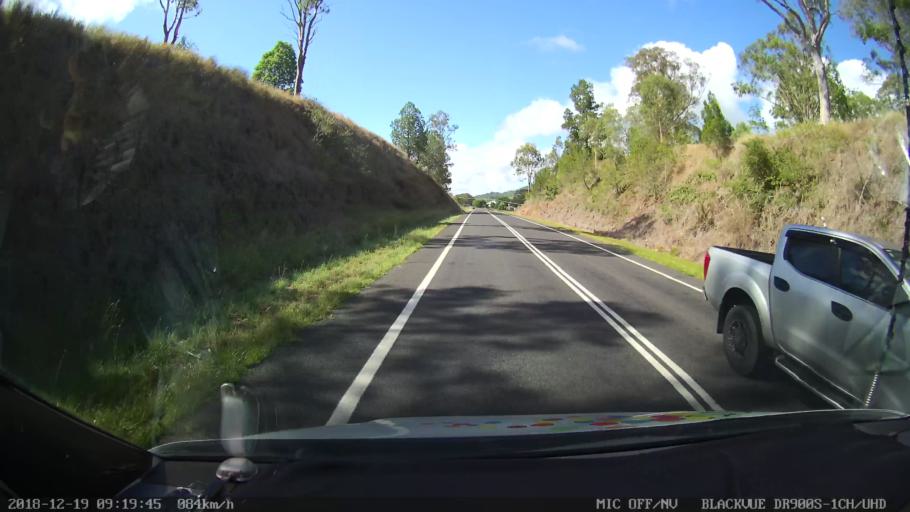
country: AU
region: New South Wales
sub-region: Kyogle
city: Kyogle
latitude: -28.5639
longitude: 152.9783
